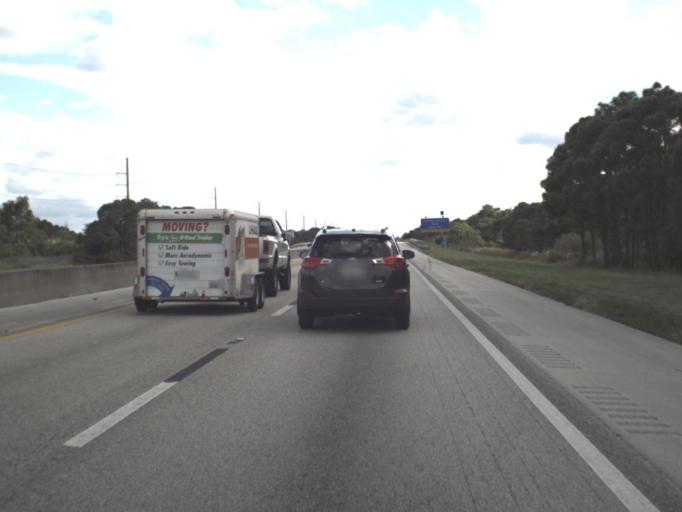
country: US
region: Florida
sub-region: Saint Lucie County
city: Port Saint Lucie
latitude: 27.2461
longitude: -80.3467
